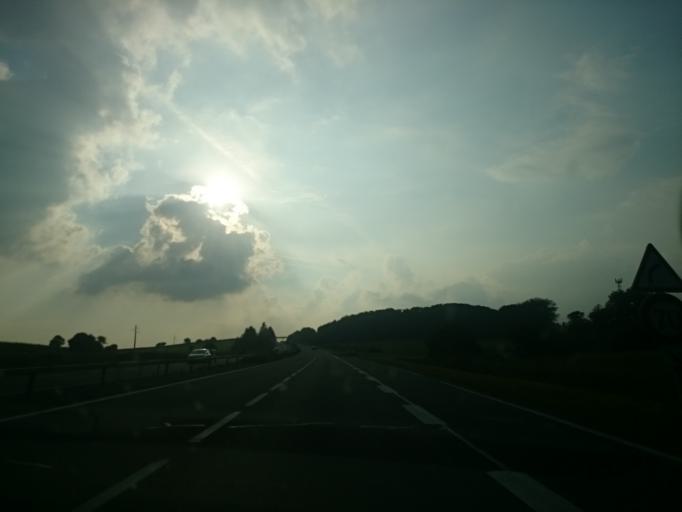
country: FR
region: Brittany
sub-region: Departement du Finistere
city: La Roche-Maurice
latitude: 48.5012
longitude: -4.1755
